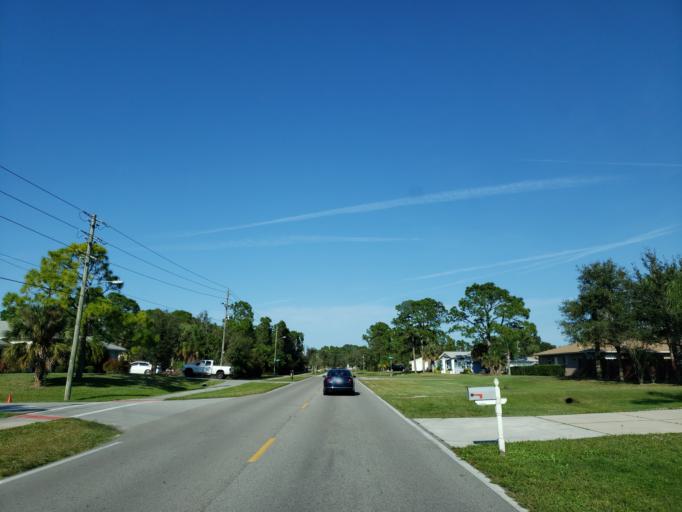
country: US
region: Florida
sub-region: Sarasota County
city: North Port
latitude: 27.0713
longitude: -82.1970
